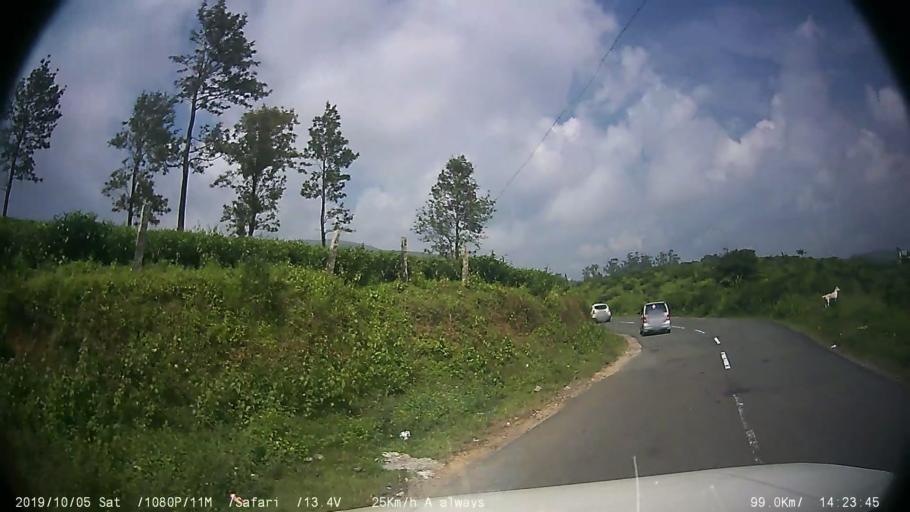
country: IN
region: Kerala
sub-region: Kottayam
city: Erattupetta
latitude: 9.5921
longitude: 76.9683
